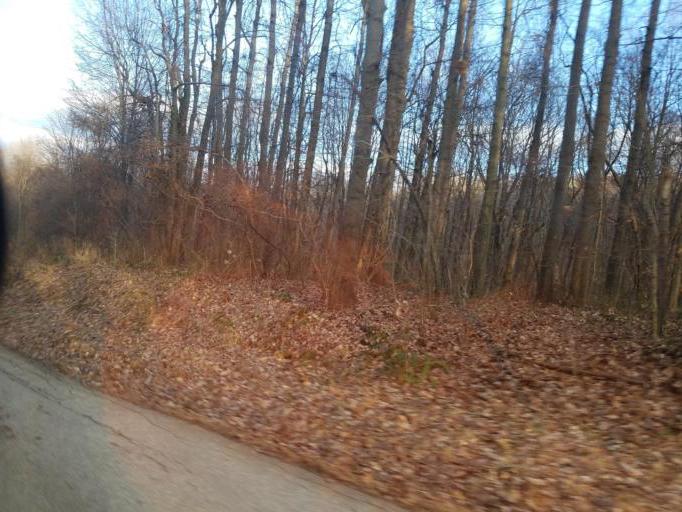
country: US
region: Ohio
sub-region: Sandusky County
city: Bellville
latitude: 40.5839
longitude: -82.4541
